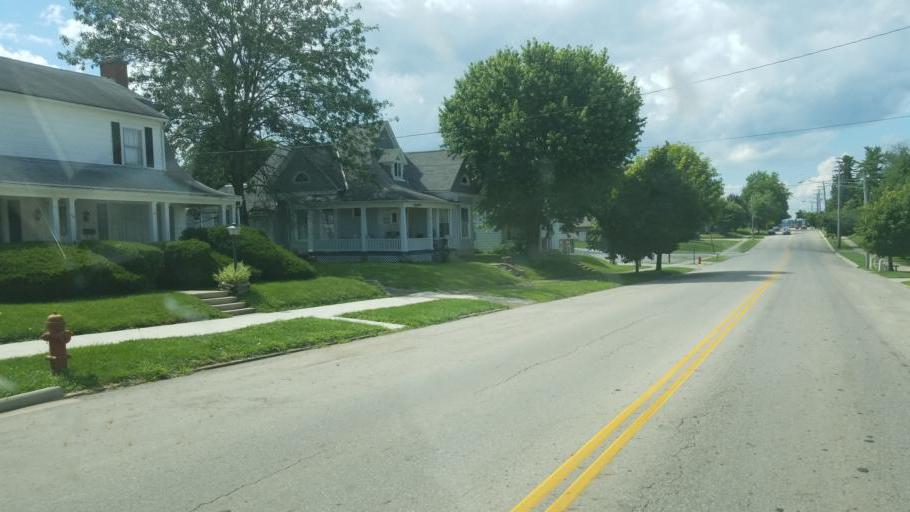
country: US
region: Ohio
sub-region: Highland County
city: Greenfield
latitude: 39.3558
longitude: -83.3845
